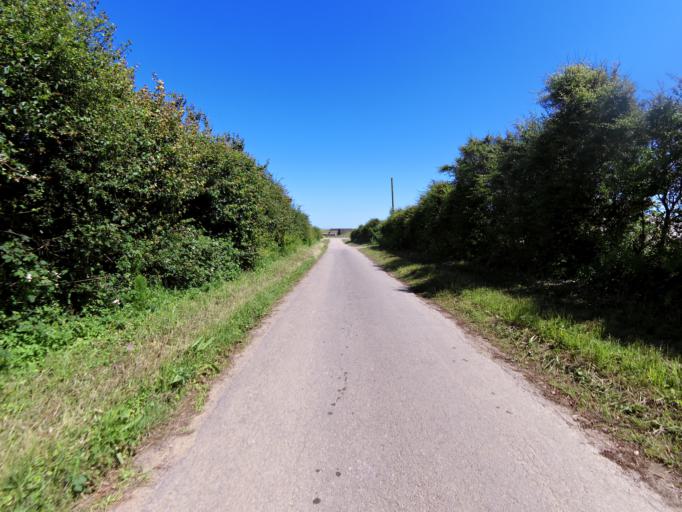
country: GB
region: England
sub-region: Suffolk
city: Felixstowe
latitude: 52.0090
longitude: 1.4320
